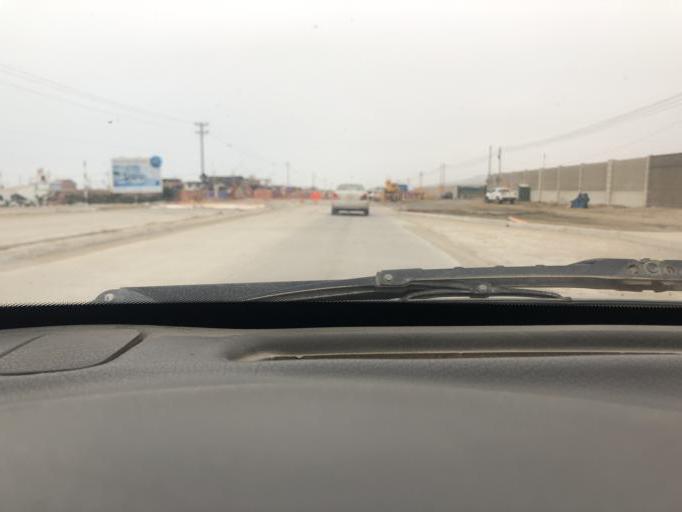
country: PE
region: Lima
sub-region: Lima
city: San Bartolo
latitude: -12.3786
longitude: -76.7801
